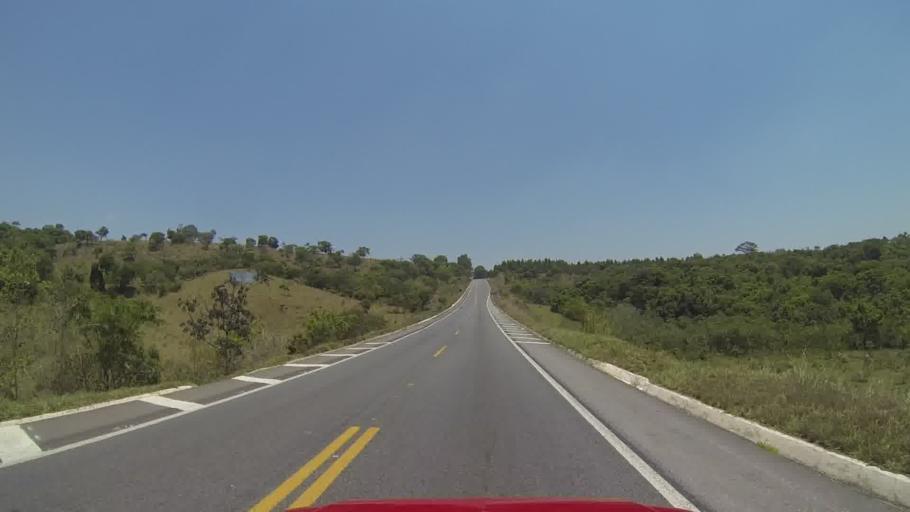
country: BR
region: Minas Gerais
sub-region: Itapecerica
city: Itapecerica
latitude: -20.2773
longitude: -45.1247
